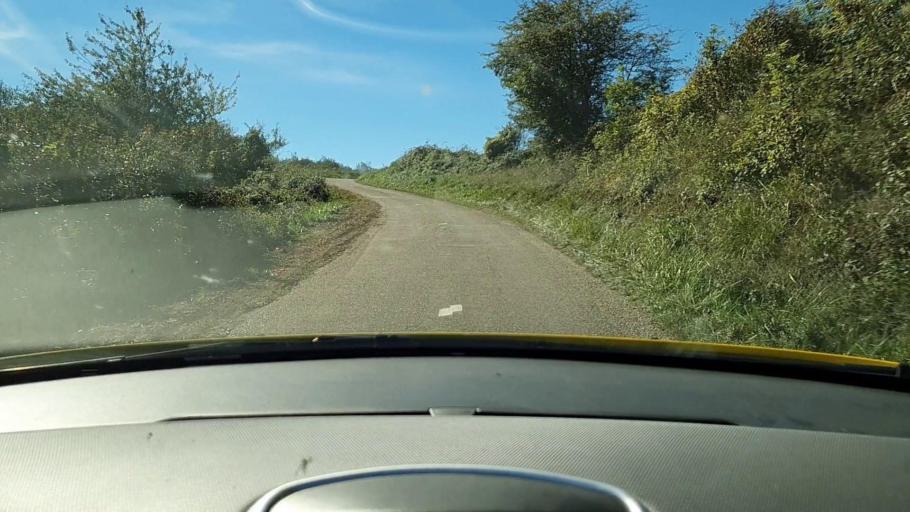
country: FR
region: Languedoc-Roussillon
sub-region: Departement du Gard
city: Aveze
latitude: 43.9607
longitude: 3.4256
